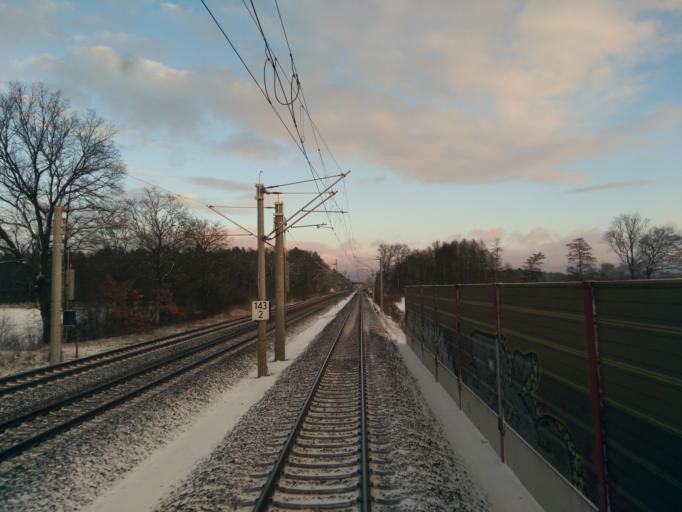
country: DE
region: Lower Saxony
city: Radbruch
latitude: 53.3157
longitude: 10.2958
